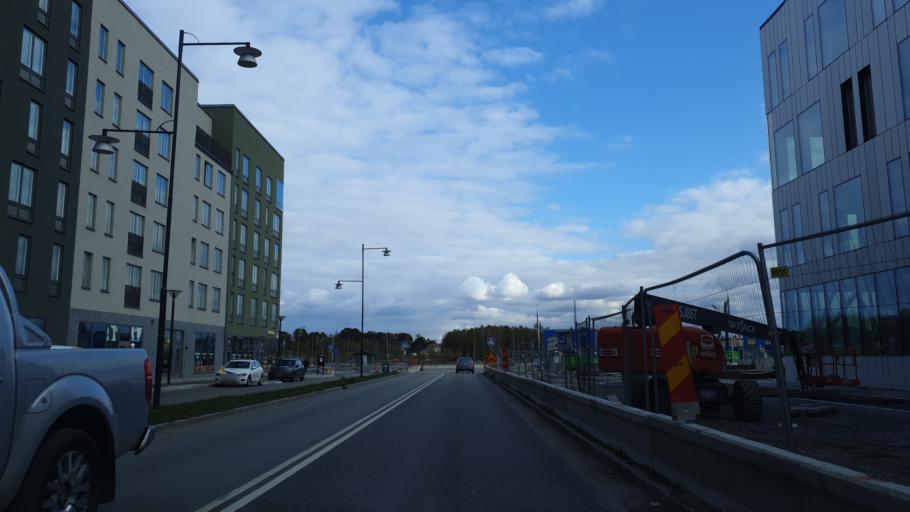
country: SE
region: Stockholm
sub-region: Jarfalla Kommun
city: Jakobsberg
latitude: 59.4110
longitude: 17.8638
